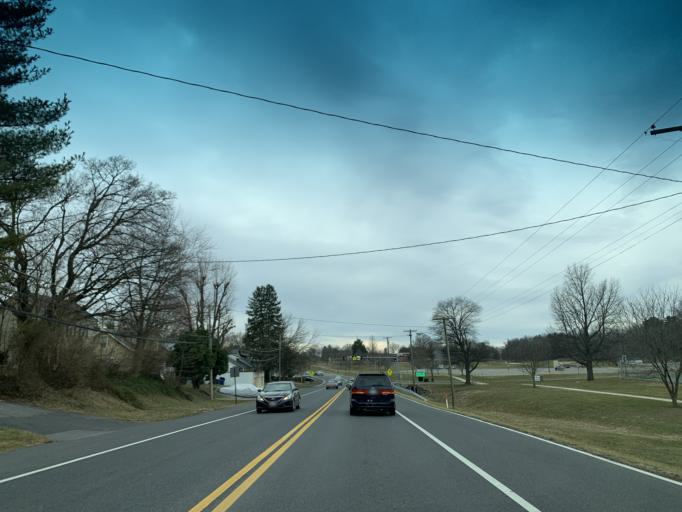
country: US
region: Maryland
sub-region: Washington County
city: Hagerstown
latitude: 39.6209
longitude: -77.7294
